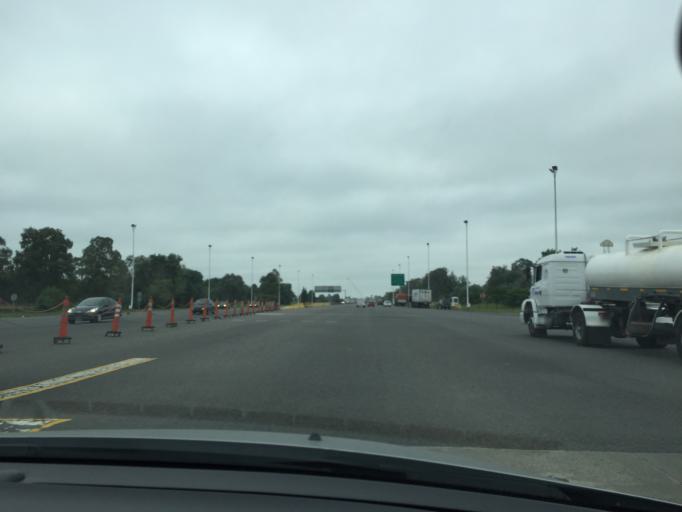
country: AR
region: Buenos Aires
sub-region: Partido de Ezeiza
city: Ezeiza
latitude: -34.8542
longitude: -58.5521
